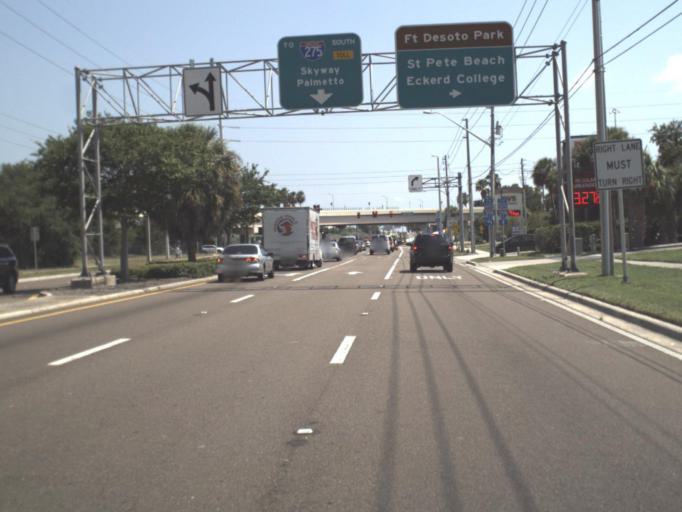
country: US
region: Florida
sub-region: Pinellas County
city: Gulfport
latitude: 27.7207
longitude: -82.6794
